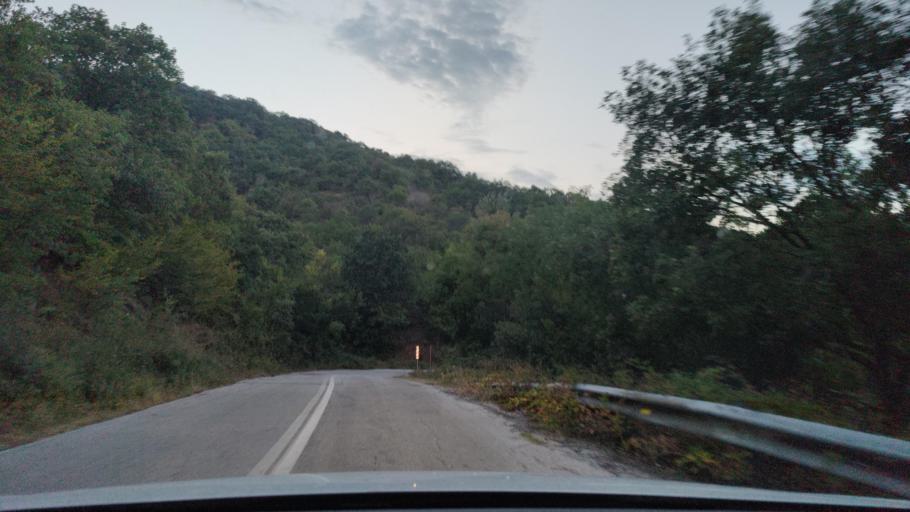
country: GR
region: Central Macedonia
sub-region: Nomos Serron
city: Chrysochorafa
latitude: 41.1696
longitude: 23.1766
